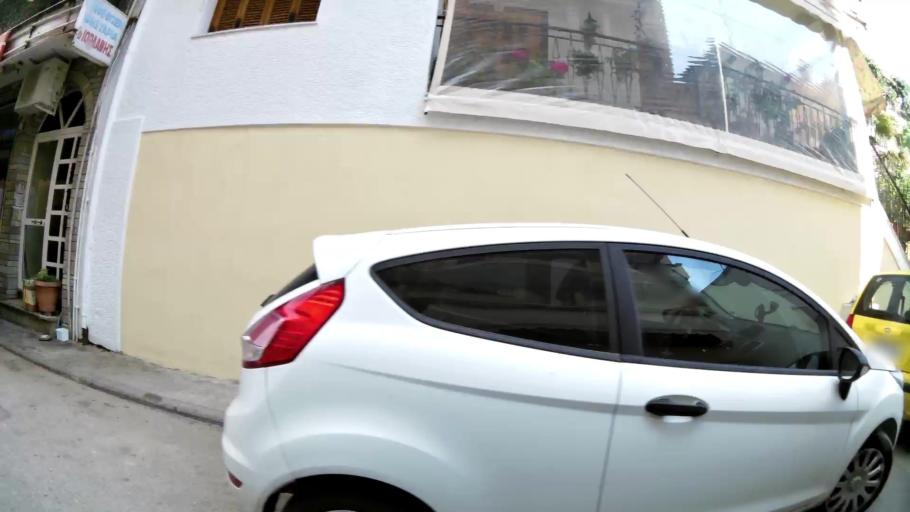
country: GR
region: Central Macedonia
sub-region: Nomos Thessalonikis
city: Polichni
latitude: 40.6620
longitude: 22.9493
